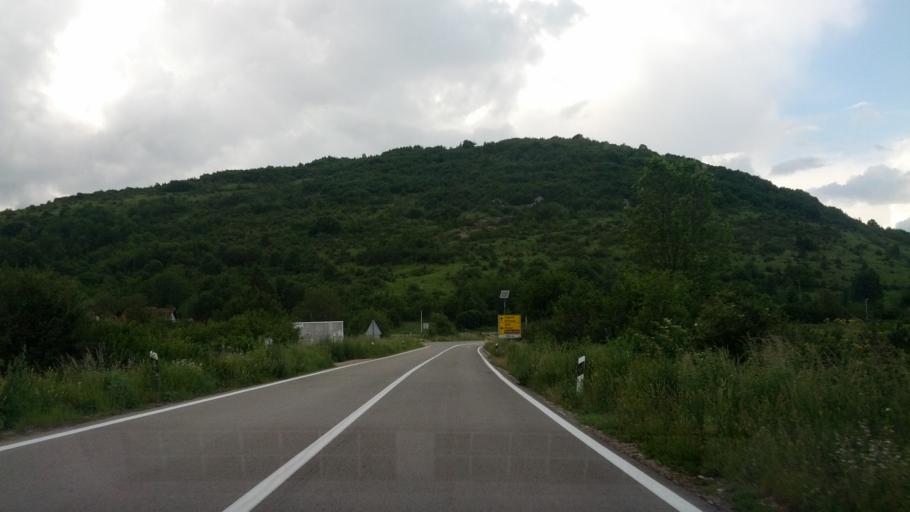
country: BA
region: Federation of Bosnia and Herzegovina
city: Izacic
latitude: 44.8800
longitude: 15.7267
